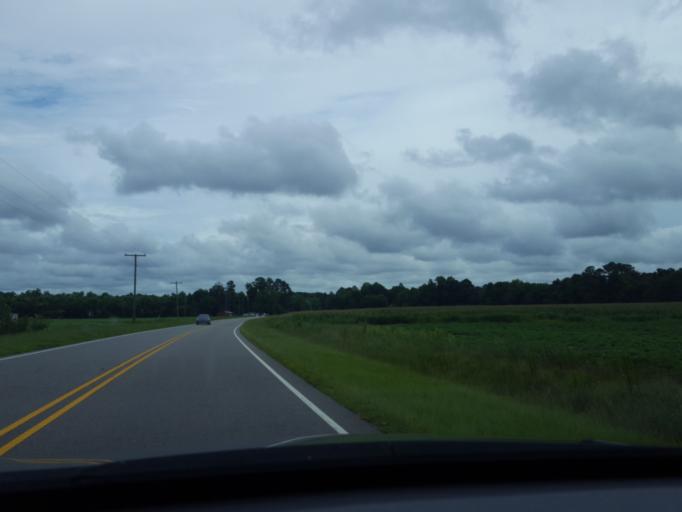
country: US
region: North Carolina
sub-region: Martin County
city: Williamston
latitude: 35.7155
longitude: -76.9855
